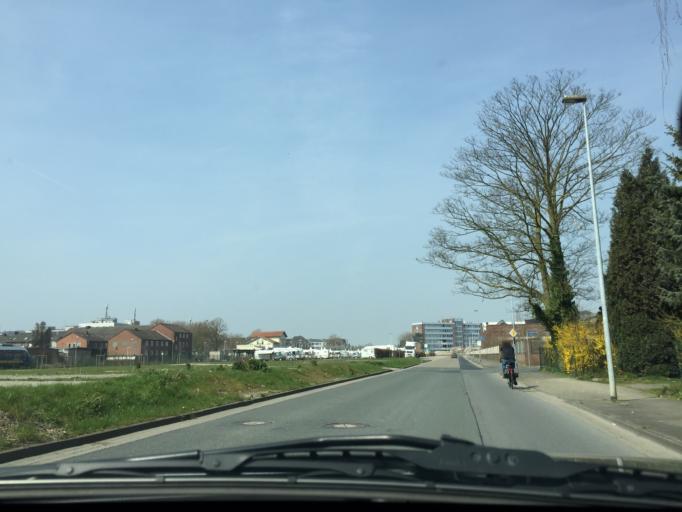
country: DE
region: North Rhine-Westphalia
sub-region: Regierungsbezirk Dusseldorf
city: Kleve
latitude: 51.7883
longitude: 6.1498
